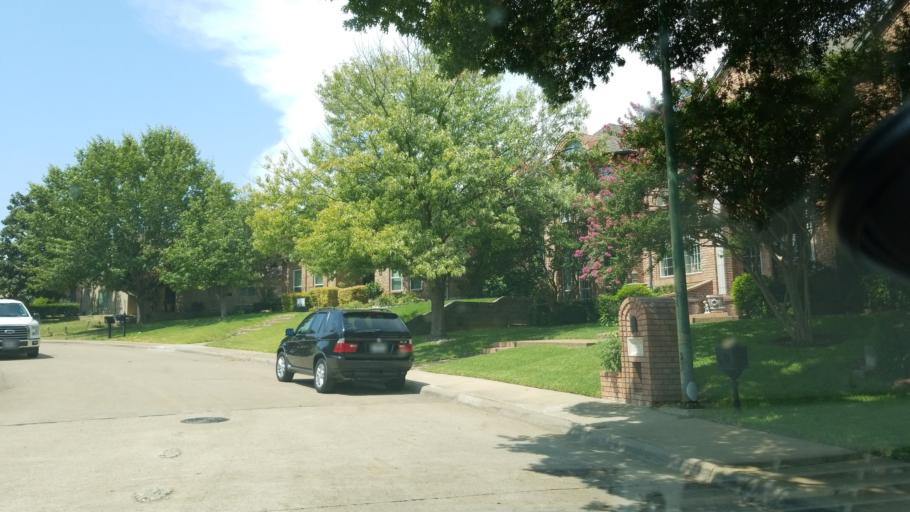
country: US
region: Texas
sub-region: Dallas County
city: Richardson
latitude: 32.8939
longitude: -96.7330
